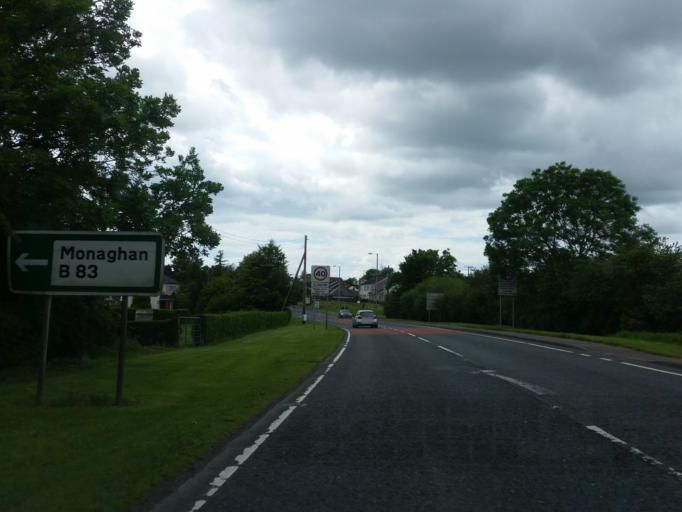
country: GB
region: Northern Ireland
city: Fivemiletown
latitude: 54.4179
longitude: -7.1572
